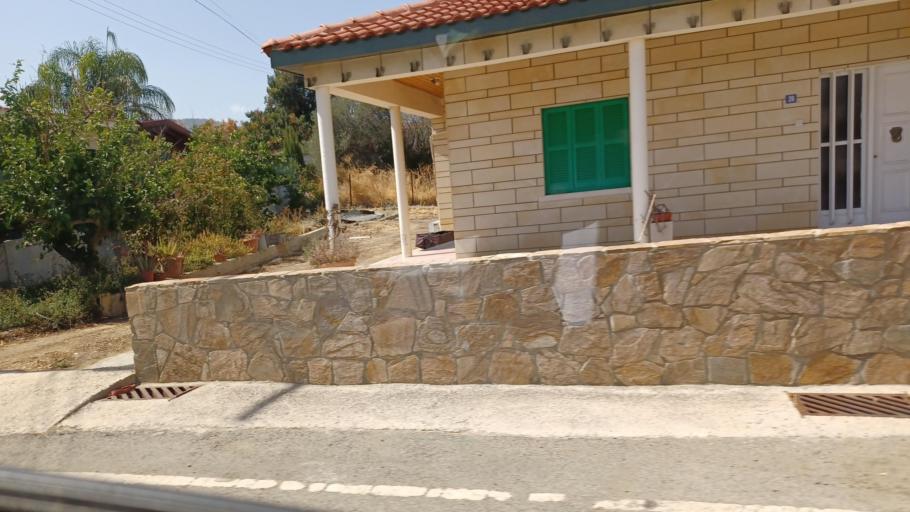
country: CY
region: Lefkosia
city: Lefka
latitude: 35.0626
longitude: 32.8877
